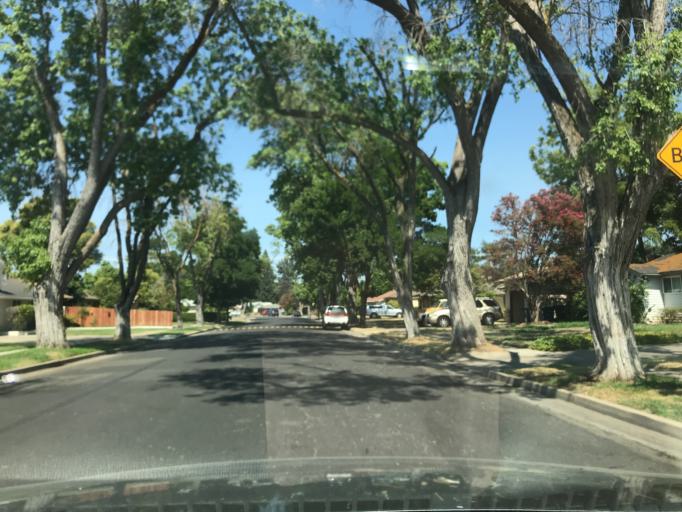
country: US
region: California
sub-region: Merced County
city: Merced
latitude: 37.3139
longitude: -120.4912
